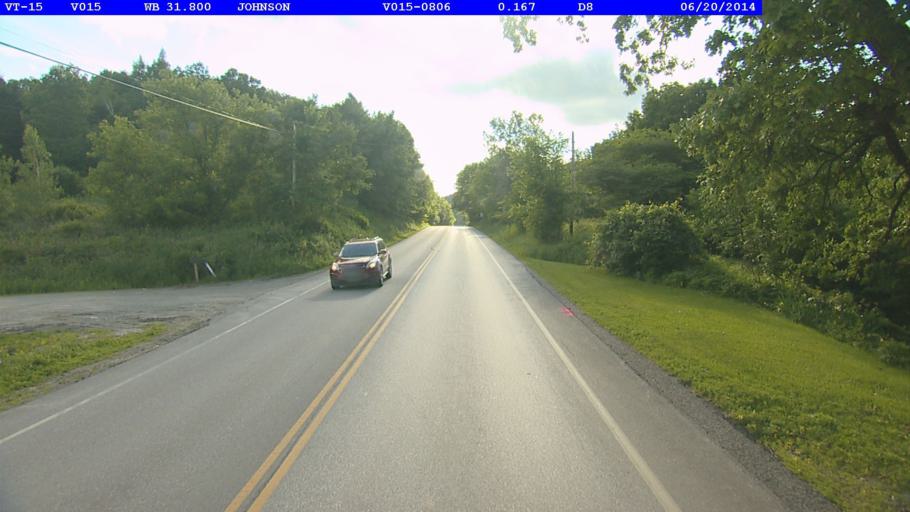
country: US
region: Vermont
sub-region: Lamoille County
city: Johnson
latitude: 44.6501
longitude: -72.7514
